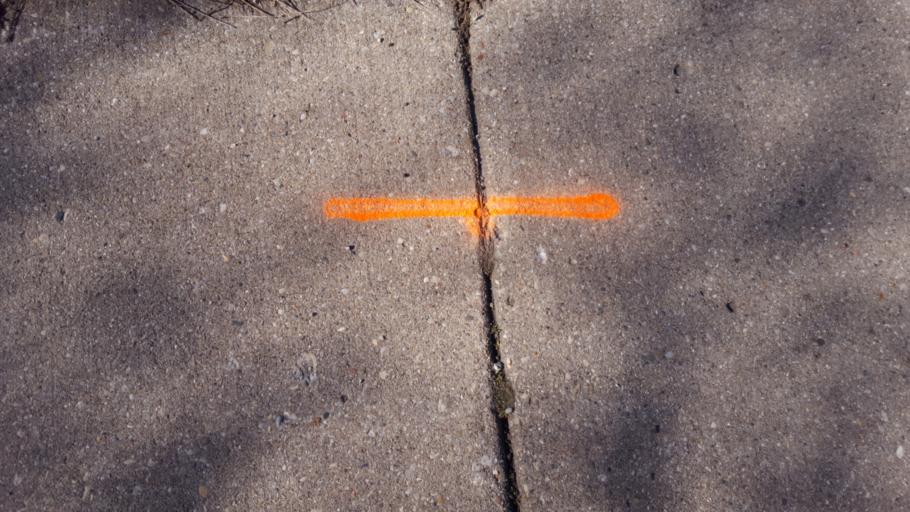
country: US
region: Illinois
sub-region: Cook County
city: Northbrook
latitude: 42.1381
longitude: -87.8356
